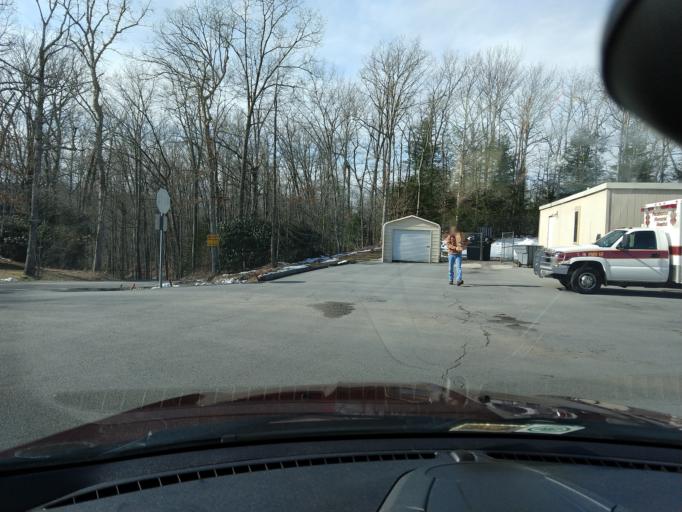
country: US
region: West Virginia
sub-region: Pocahontas County
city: Marlinton
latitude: 38.2005
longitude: -80.1089
